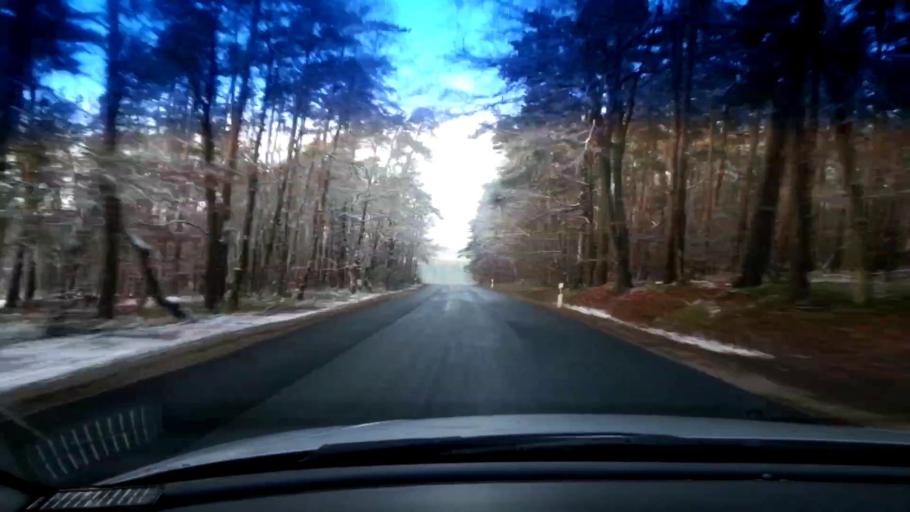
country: DE
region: Bavaria
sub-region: Regierungsbezirk Mittelfranken
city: Adelsdorf
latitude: 49.7665
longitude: 10.8936
